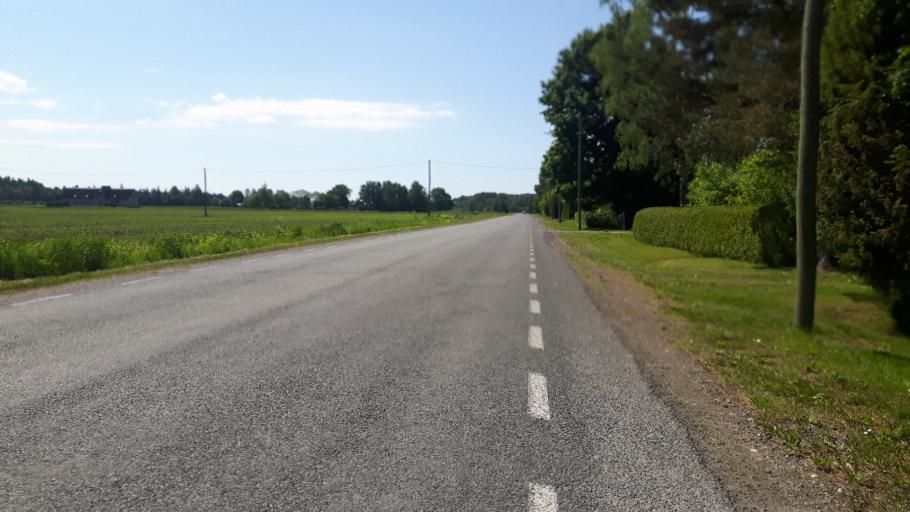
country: EE
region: Paernumaa
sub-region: Vaendra vald (alev)
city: Vandra
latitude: 58.6387
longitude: 25.0247
